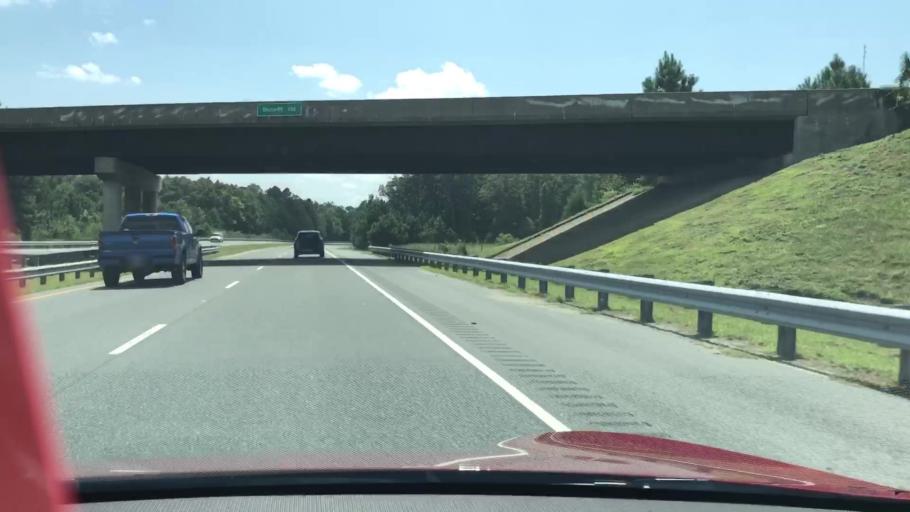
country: US
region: North Carolina
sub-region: Currituck County
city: Moyock
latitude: 36.6327
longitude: -76.2162
